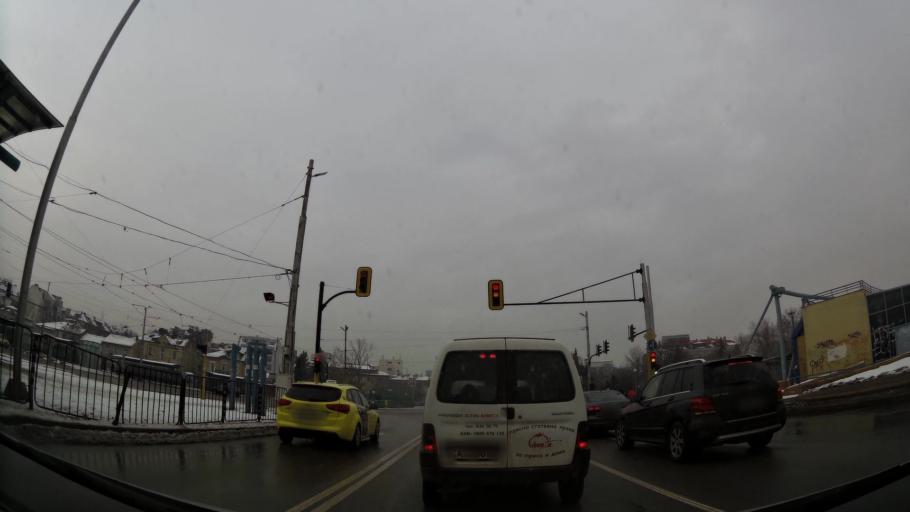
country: BG
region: Sofia-Capital
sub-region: Stolichna Obshtina
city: Sofia
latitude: 42.7114
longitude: 23.3198
